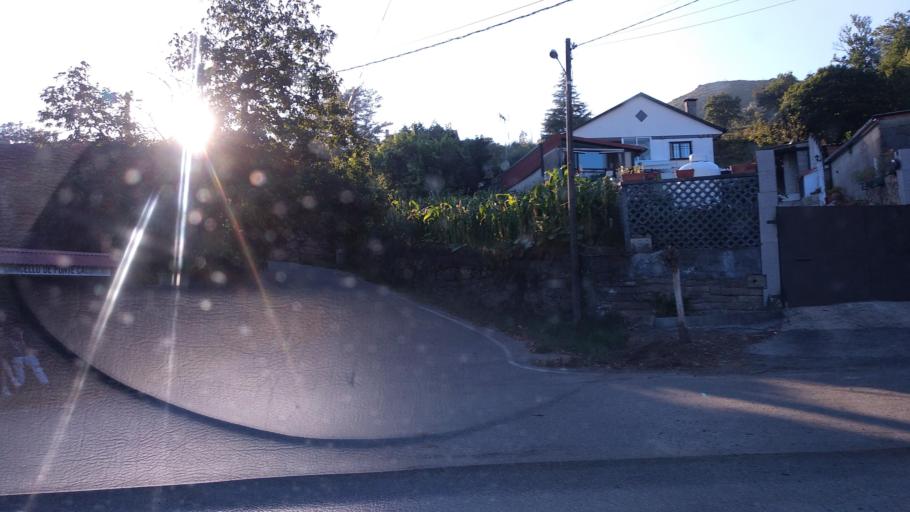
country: ES
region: Galicia
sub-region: Provincia de Pontevedra
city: Ponte Caldelas
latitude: 42.3589
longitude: -8.4926
